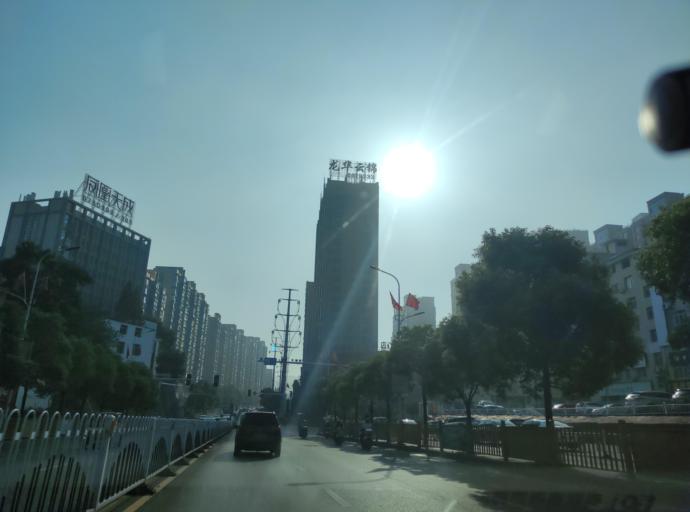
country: CN
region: Jiangxi Sheng
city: Pingxiang
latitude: 27.6336
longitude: 113.8624
